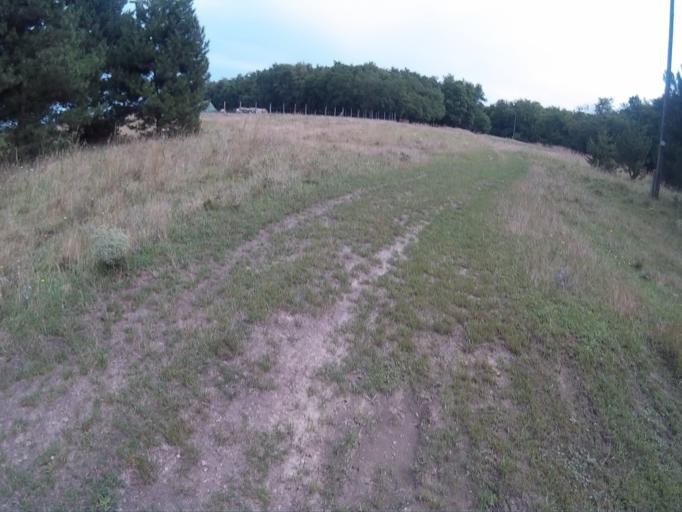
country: HU
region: Veszprem
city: Papa
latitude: 47.2833
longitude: 17.5761
